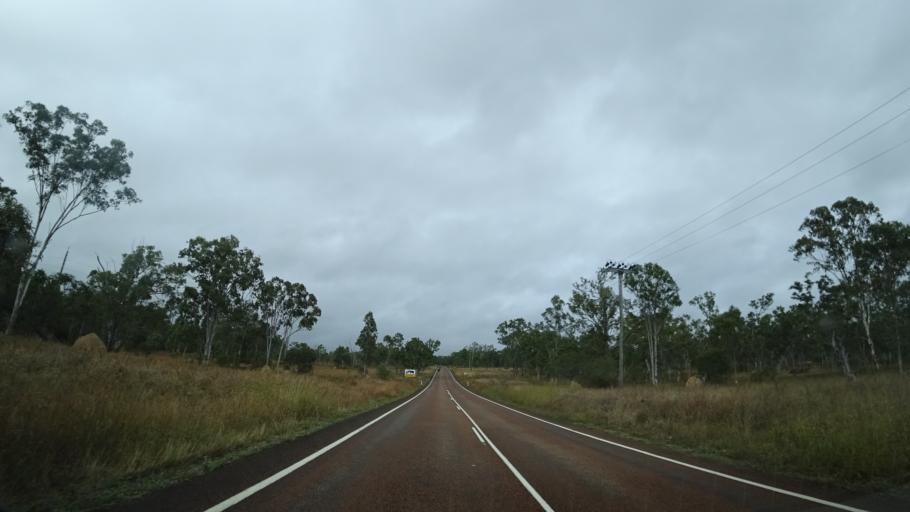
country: AU
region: Queensland
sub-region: Tablelands
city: Ravenshoe
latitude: -17.6709
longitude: 145.2378
